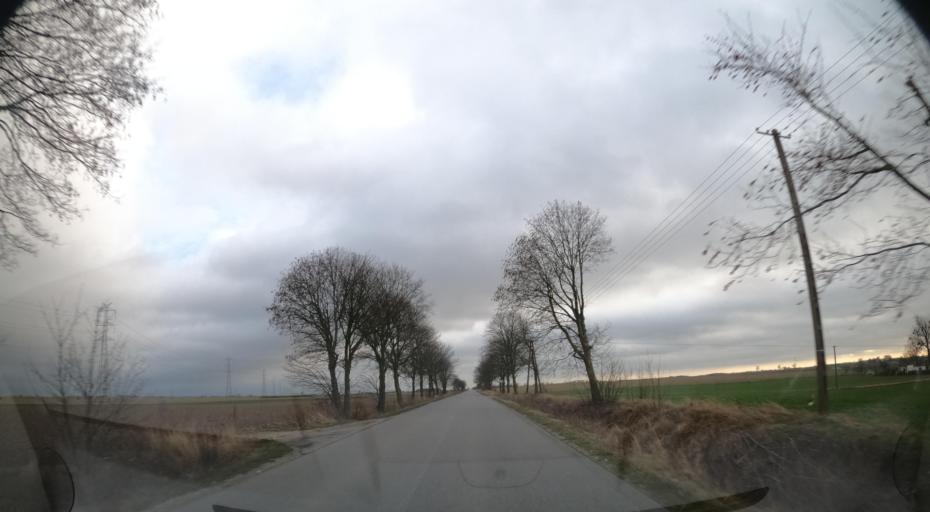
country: PL
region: Kujawsko-Pomorskie
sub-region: Powiat nakielski
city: Sadki
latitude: 53.1760
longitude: 17.4194
